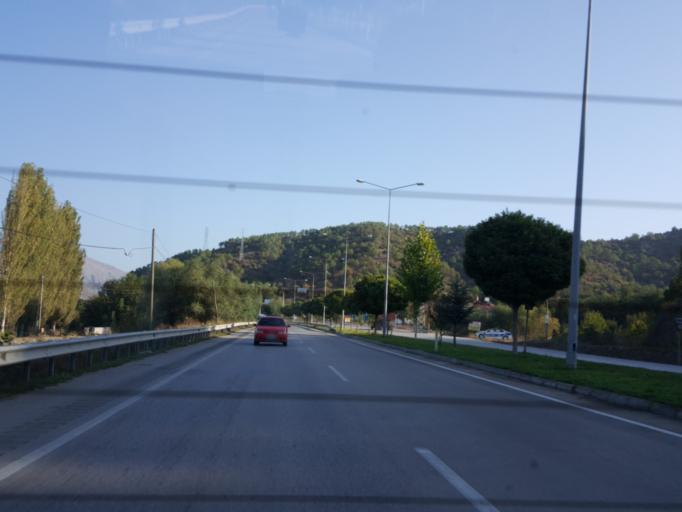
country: TR
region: Amasya
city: Amasya
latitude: 40.5769
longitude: 35.7889
